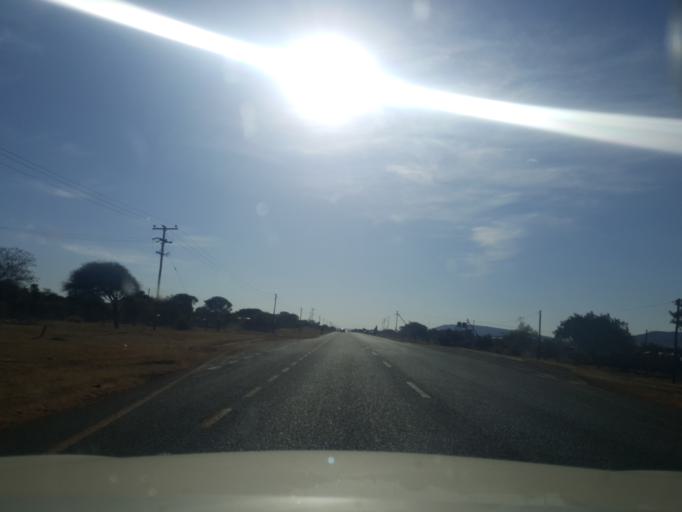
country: ZA
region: North-West
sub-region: Ngaka Modiri Molema District Municipality
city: Zeerust
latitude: -25.4858
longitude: 25.9183
